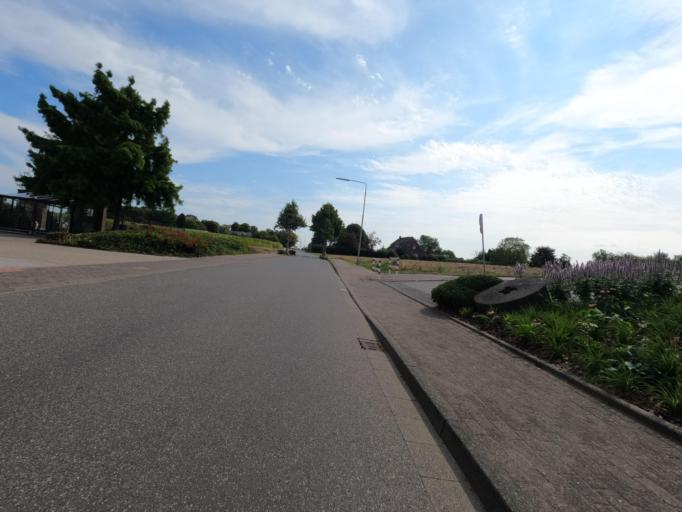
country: DE
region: North Rhine-Westphalia
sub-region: Regierungsbezirk Koln
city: Waldfeucht
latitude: 51.0570
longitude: 6.0436
